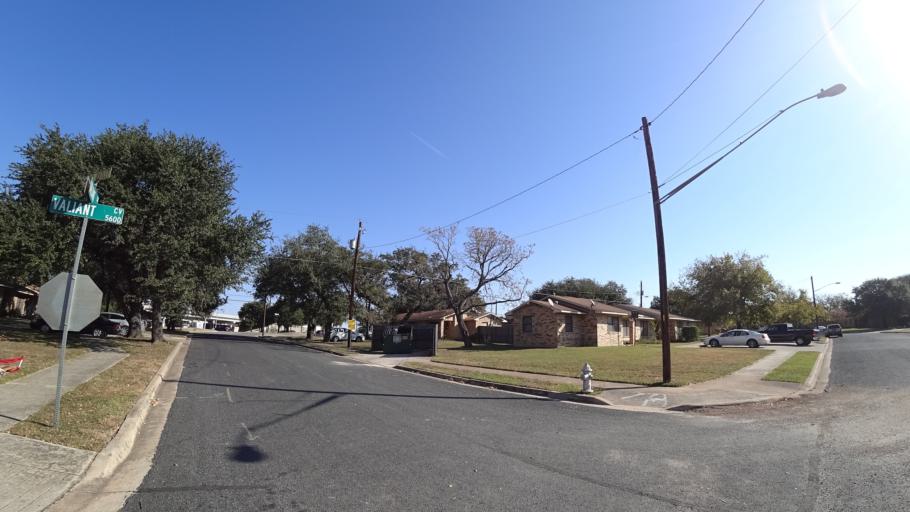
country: US
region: Texas
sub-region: Travis County
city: Barton Creek
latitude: 30.2340
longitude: -97.8525
